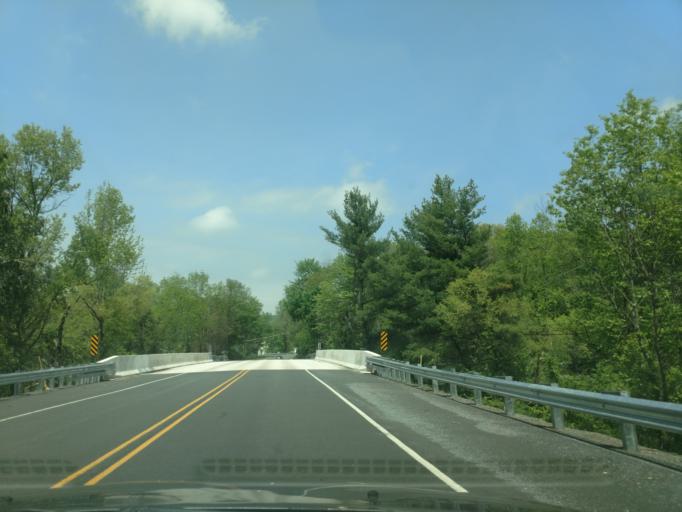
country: US
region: Pennsylvania
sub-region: Berks County
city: Birdsboro
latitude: 40.2253
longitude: -75.8514
